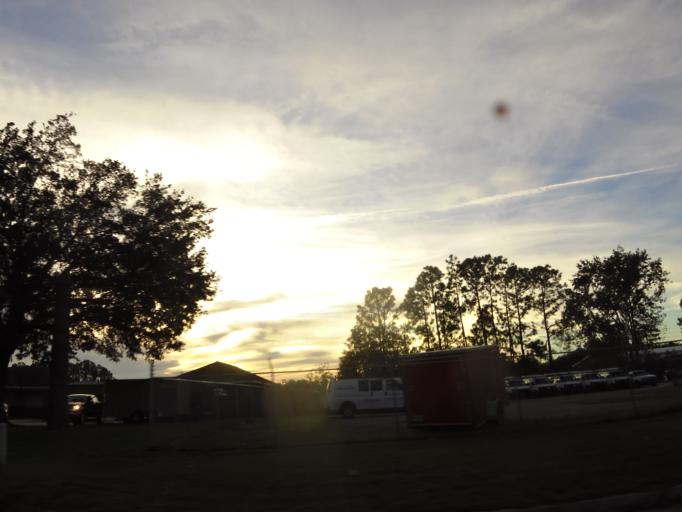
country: US
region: Florida
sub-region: Saint Johns County
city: Fruit Cove
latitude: 30.1572
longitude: -81.5367
